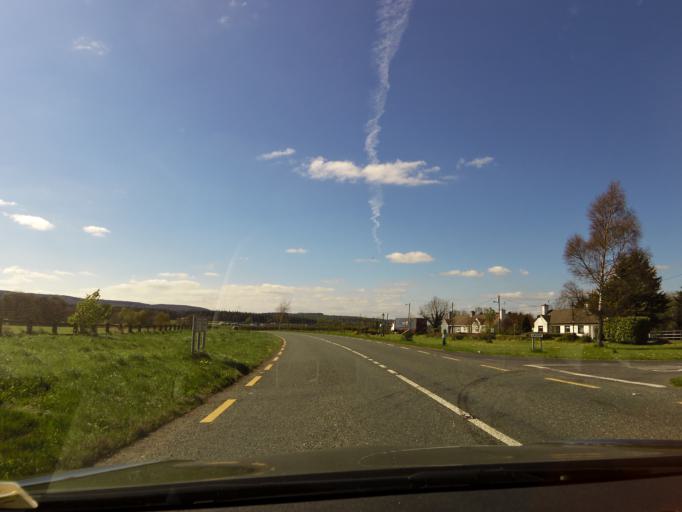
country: IE
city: Ballylinan
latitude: 53.0026
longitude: -7.0575
